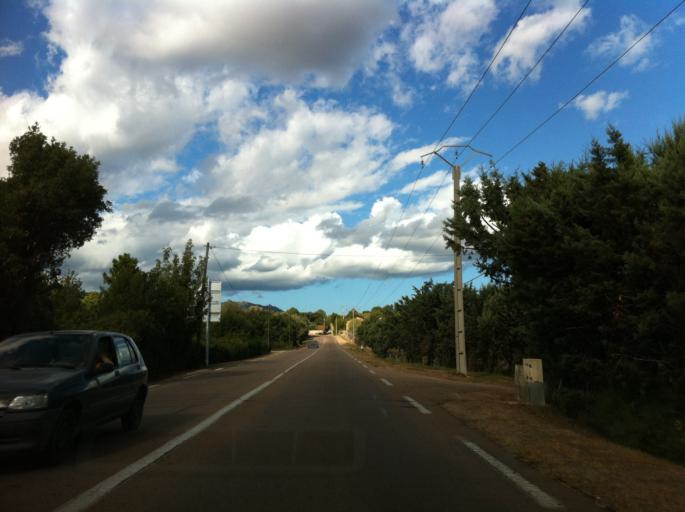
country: FR
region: Corsica
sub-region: Departement de la Corse-du-Sud
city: Porto-Vecchio
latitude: 41.6297
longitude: 9.2907
